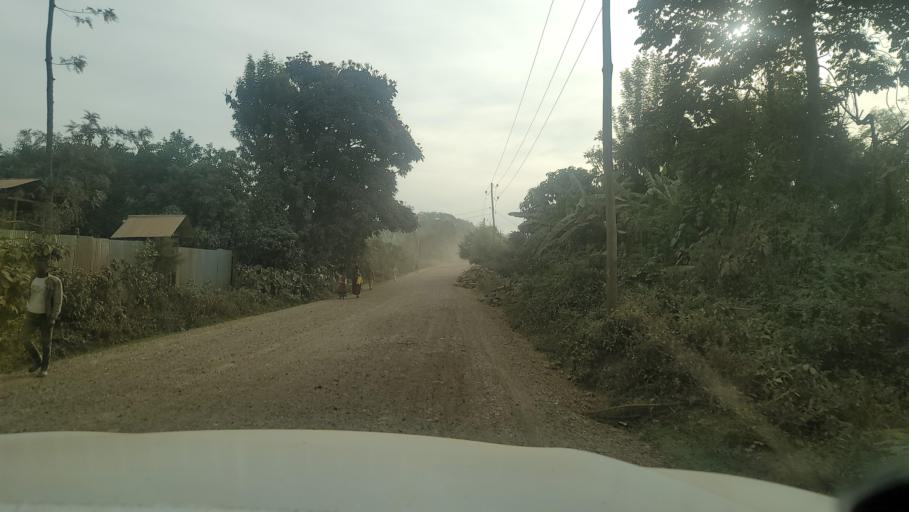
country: ET
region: Oromiya
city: Agaro
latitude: 7.8407
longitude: 36.5590
